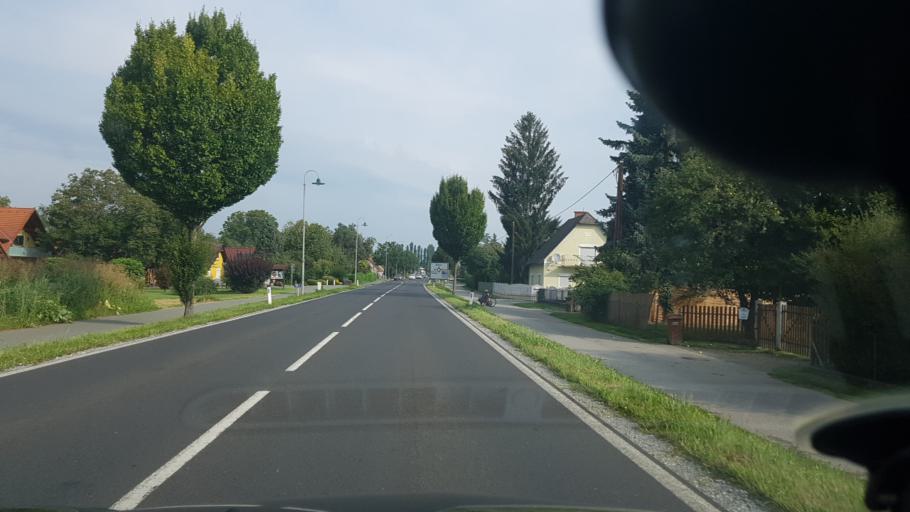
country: AT
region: Styria
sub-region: Politischer Bezirk Leibnitz
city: Kaindorf an der Sulm
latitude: 46.8000
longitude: 15.5566
